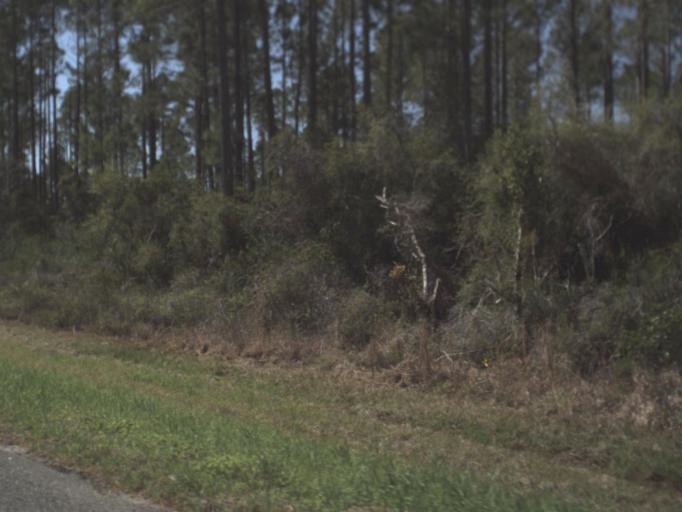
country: US
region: Florida
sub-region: Leon County
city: Woodville
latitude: 30.2979
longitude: -84.0480
